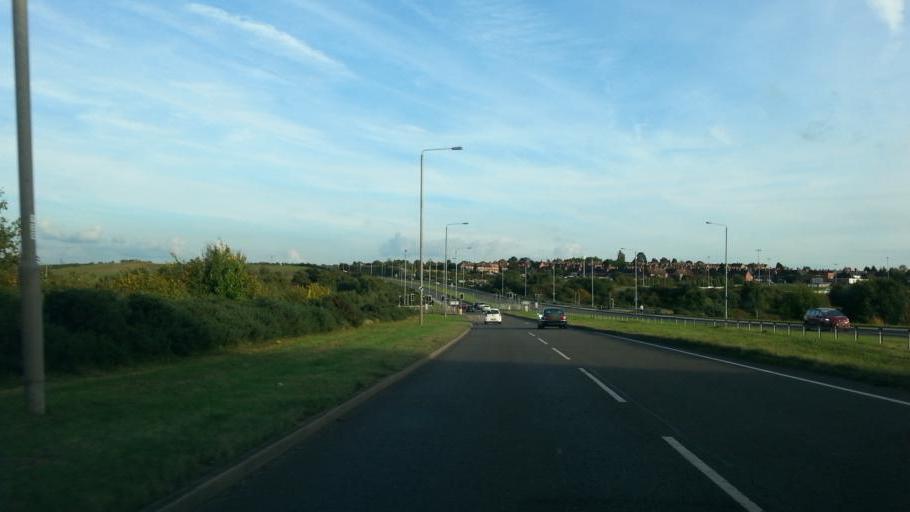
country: GB
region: England
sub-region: Nottinghamshire
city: Rainworth
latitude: 53.1233
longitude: -1.1191
